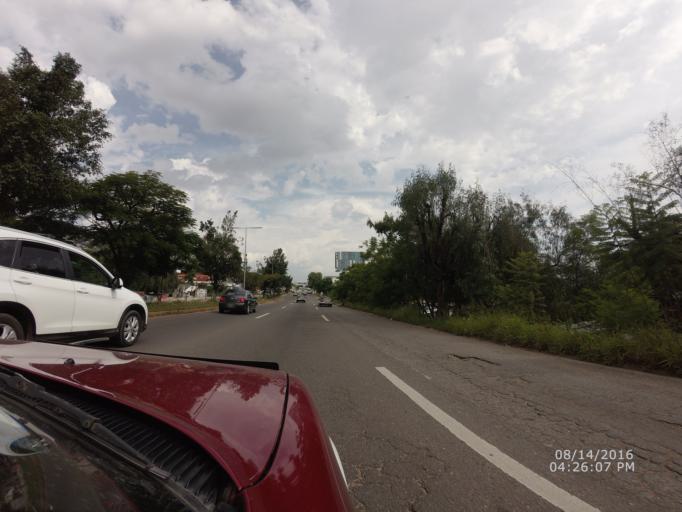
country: MX
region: Oaxaca
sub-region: Santa Maria Atzompa
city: San Jeronimo Yahuiche
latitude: 17.0955
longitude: -96.7488
